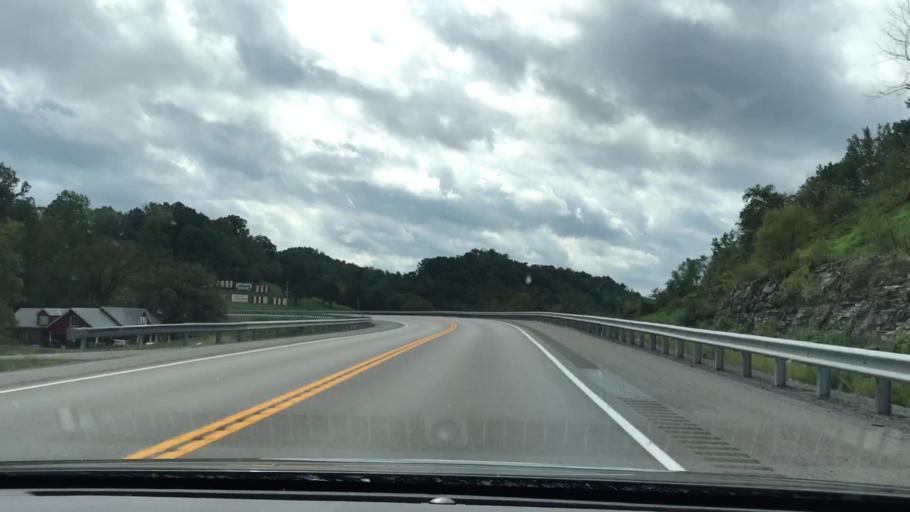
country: US
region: Kentucky
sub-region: Cumberland County
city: Burkesville
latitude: 36.7946
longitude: -85.4130
